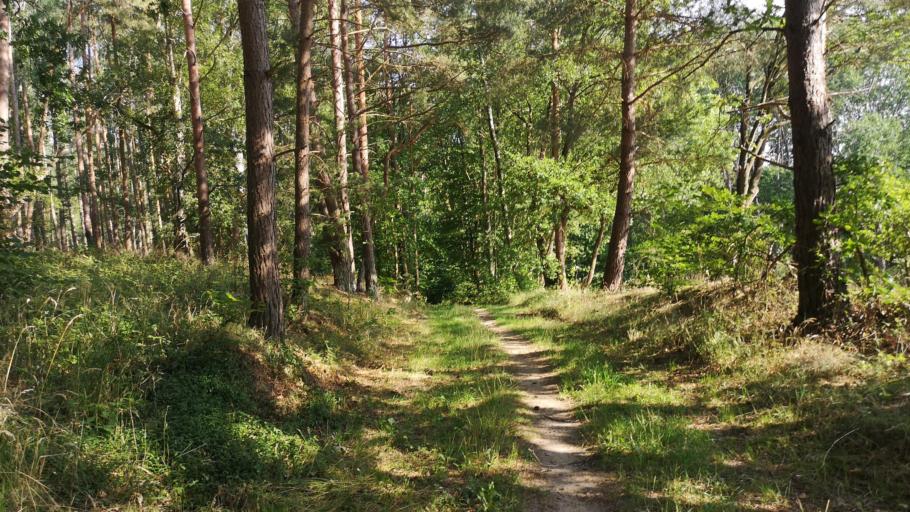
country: DE
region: Lower Saxony
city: Dahlenburg
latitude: 53.2118
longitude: 10.7174
